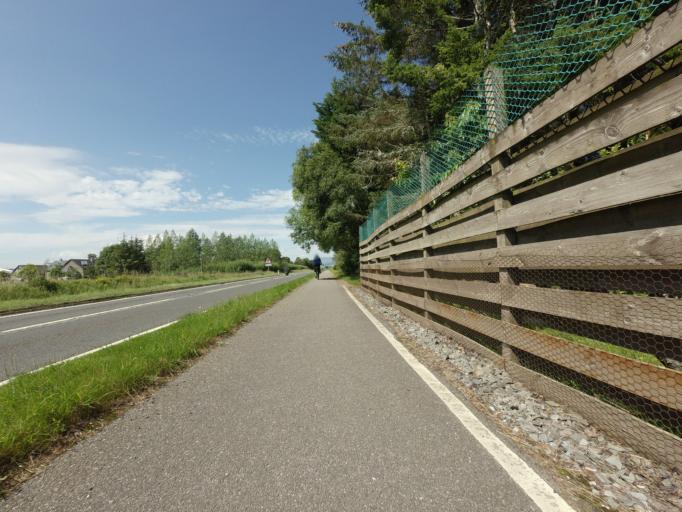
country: GB
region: Scotland
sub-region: Highland
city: Conon Bridge
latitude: 57.5465
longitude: -4.3869
